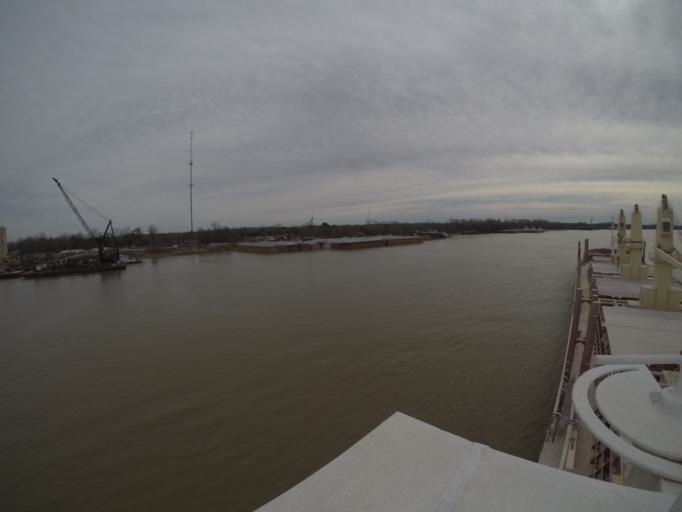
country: US
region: Louisiana
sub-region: Saint John the Baptist Parish
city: Laplace
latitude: 30.0479
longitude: -90.4786
